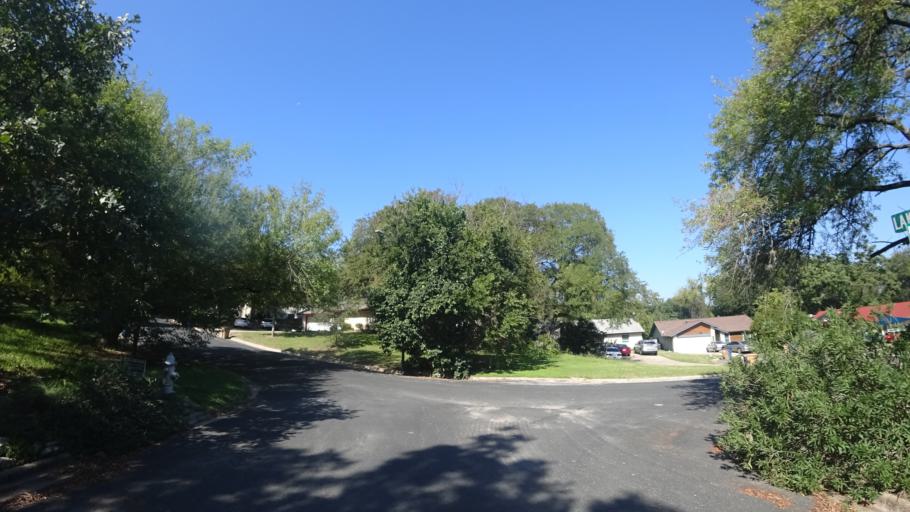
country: US
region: Texas
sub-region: Travis County
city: Austin
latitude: 30.3122
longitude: -97.6729
